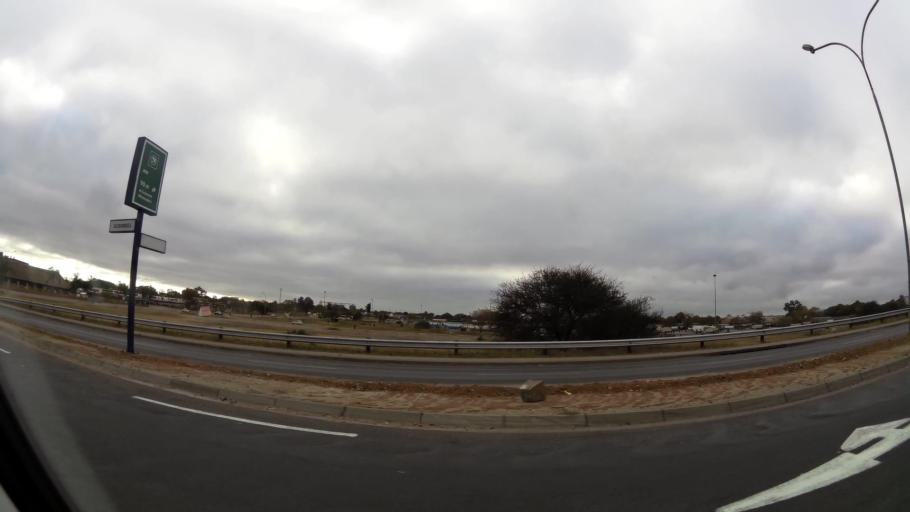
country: ZA
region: Limpopo
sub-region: Capricorn District Municipality
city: Polokwane
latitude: -23.9001
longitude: 29.4398
